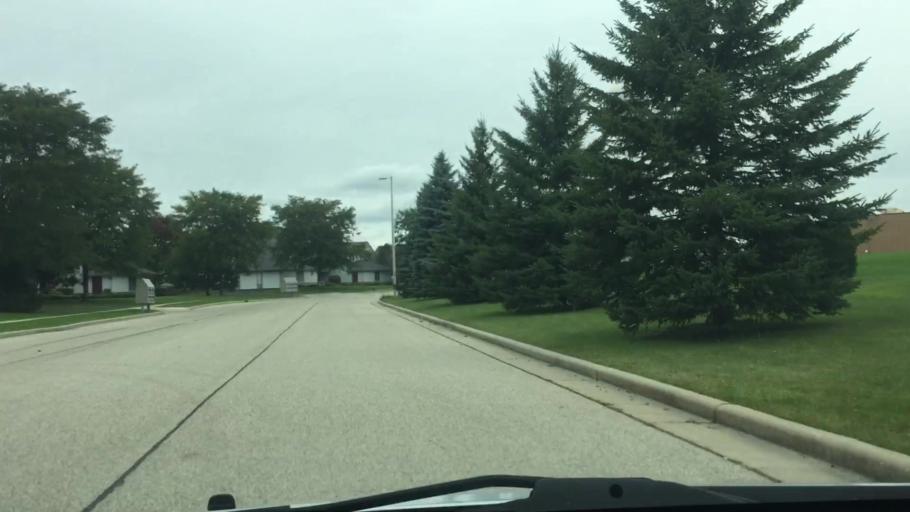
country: US
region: Wisconsin
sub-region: Waukesha County
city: Pewaukee
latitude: 43.0930
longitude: -88.2786
